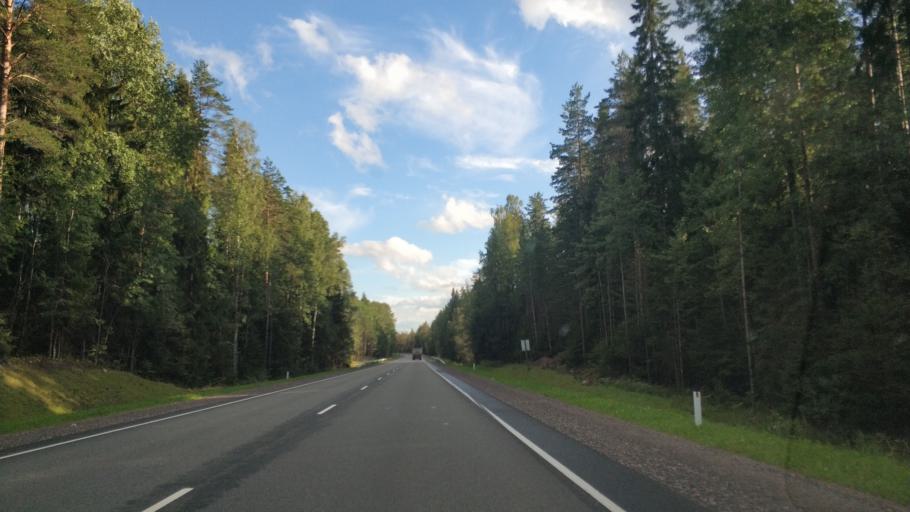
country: RU
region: Leningrad
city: Priozersk
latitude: 60.8964
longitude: 30.1596
